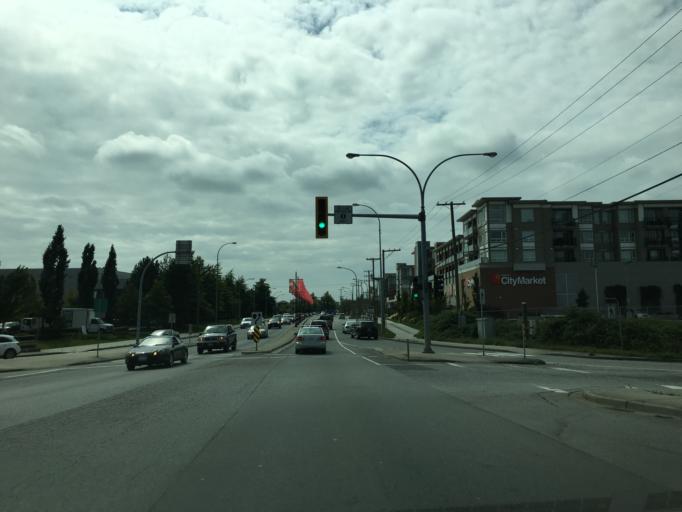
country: CA
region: British Columbia
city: Ladner
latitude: 49.1335
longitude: -123.0882
